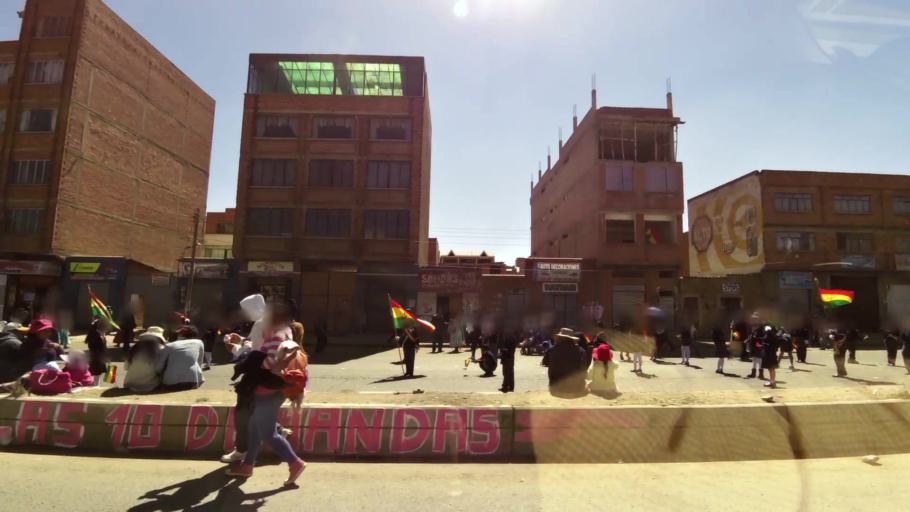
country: BO
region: La Paz
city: La Paz
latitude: -16.4953
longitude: -68.1914
